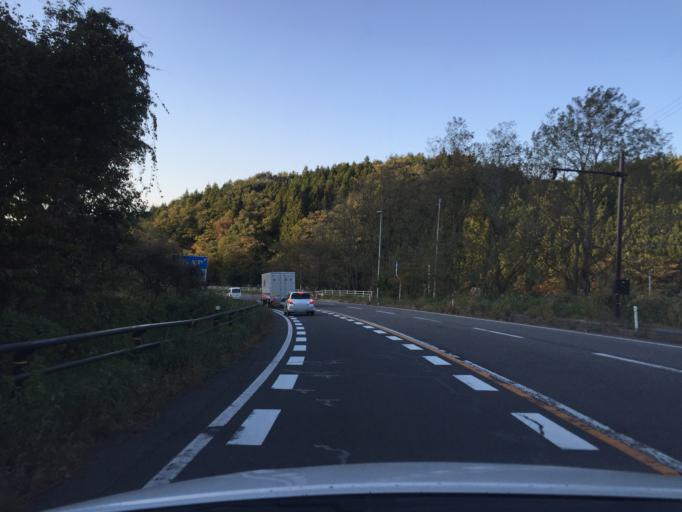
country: JP
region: Fukushima
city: Ishikawa
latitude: 37.2753
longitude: 140.5502
